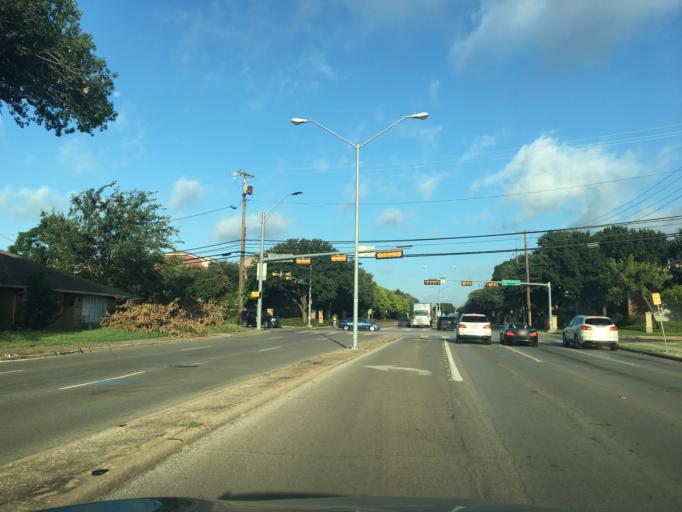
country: US
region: Texas
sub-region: Dallas County
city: Highland Park
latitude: 32.8510
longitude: -96.7599
